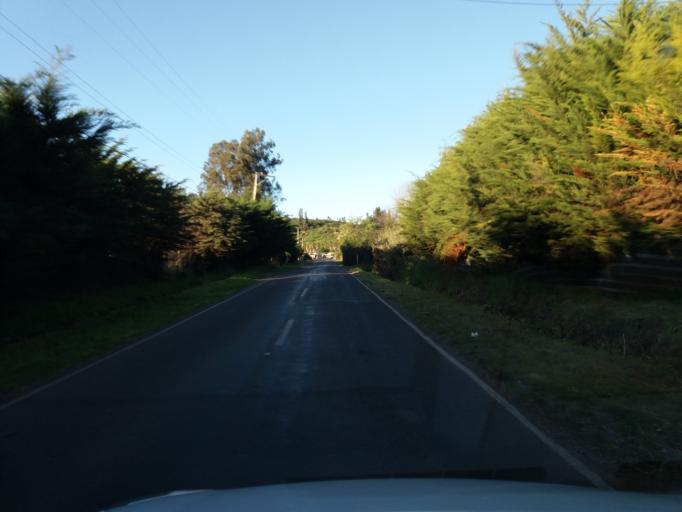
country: CL
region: Valparaiso
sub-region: Provincia de Quillota
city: Quillota
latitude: -32.8968
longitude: -71.2960
